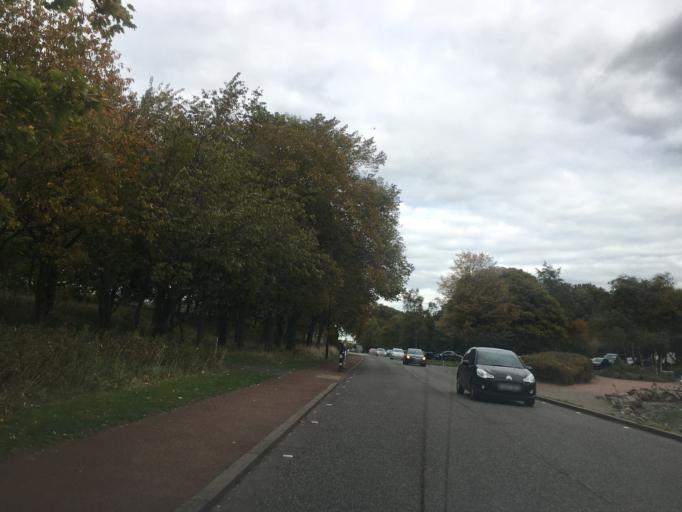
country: GB
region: Scotland
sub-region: West Lothian
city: Seafield
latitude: 55.9529
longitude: -3.1612
